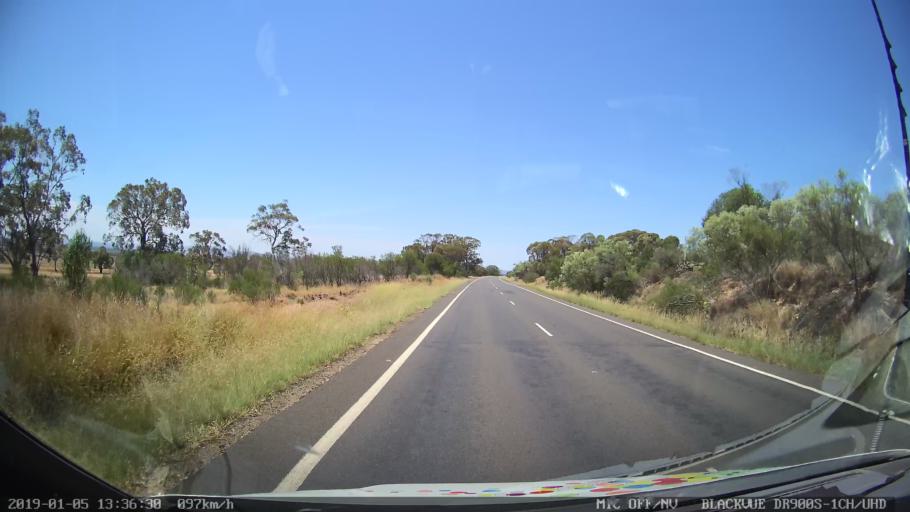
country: AU
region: New South Wales
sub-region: Gunnedah
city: Gunnedah
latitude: -30.9845
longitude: 150.1657
